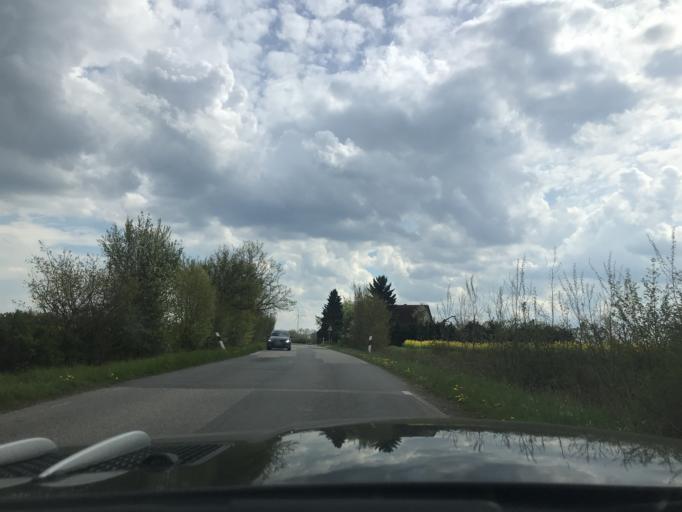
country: DE
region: Schleswig-Holstein
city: Timmendorfer Strand
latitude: 53.9550
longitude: 10.7898
